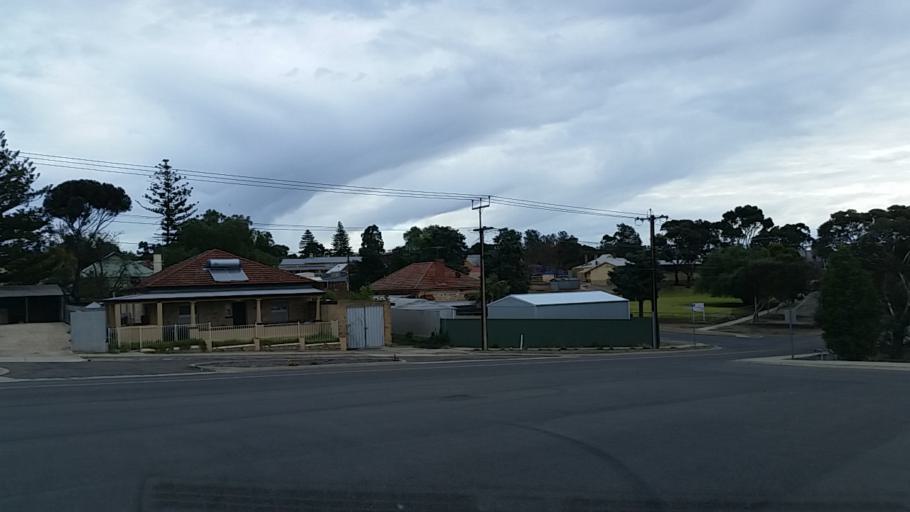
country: AU
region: South Australia
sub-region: Murray Bridge
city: Murray Bridge
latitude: -35.1157
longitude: 139.2733
